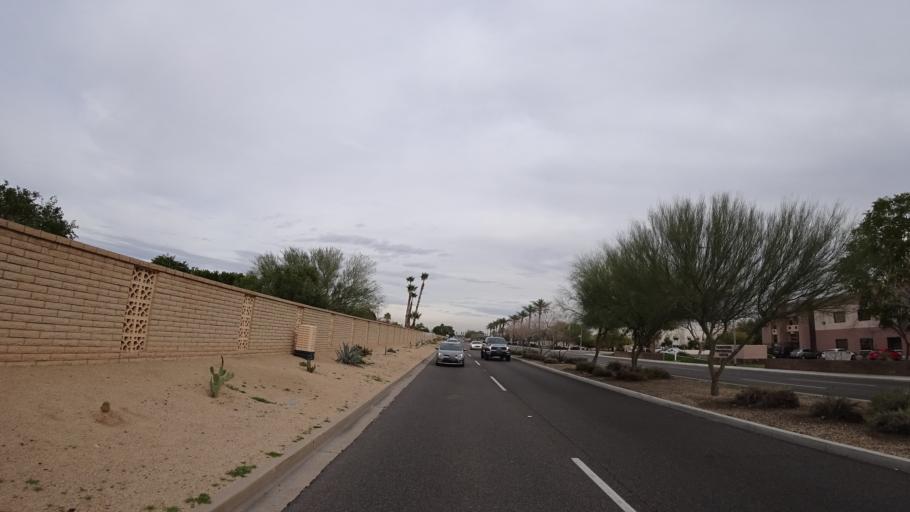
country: US
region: Arizona
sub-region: Maricopa County
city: Sun City
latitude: 33.6096
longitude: -112.2610
